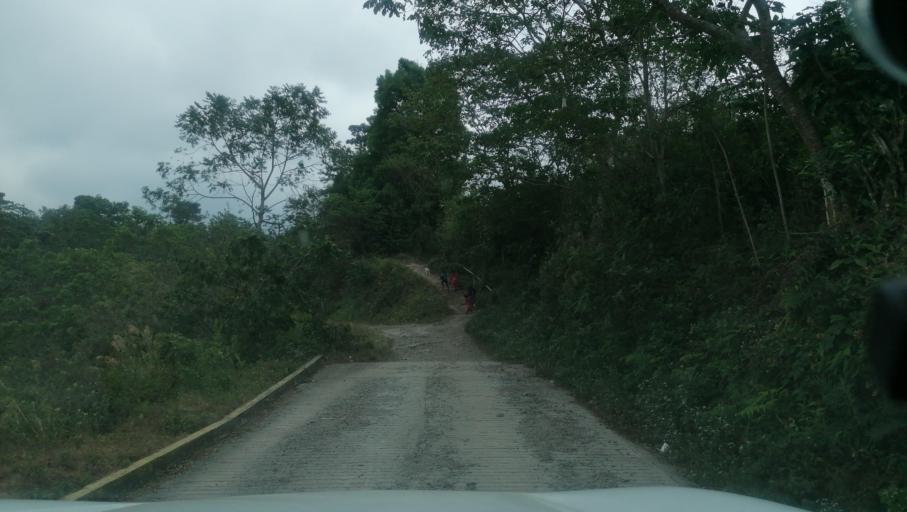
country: GT
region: San Marcos
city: Sibinal
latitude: 15.1664
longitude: -92.1620
